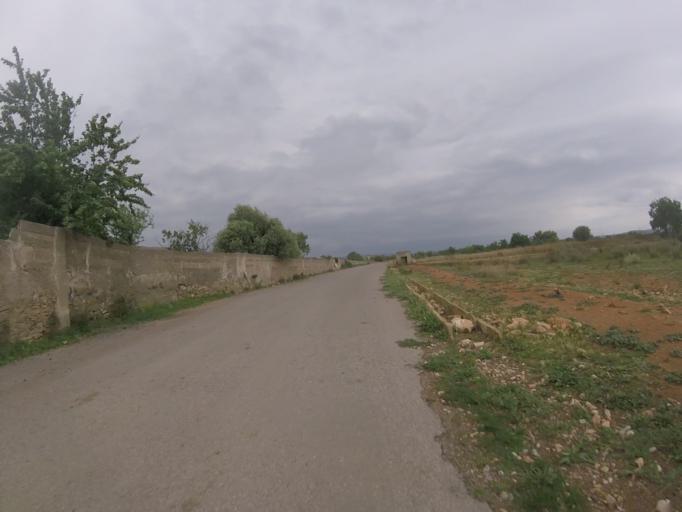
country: ES
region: Valencia
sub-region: Provincia de Castello
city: Torreblanca
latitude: 40.2138
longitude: 0.2404
